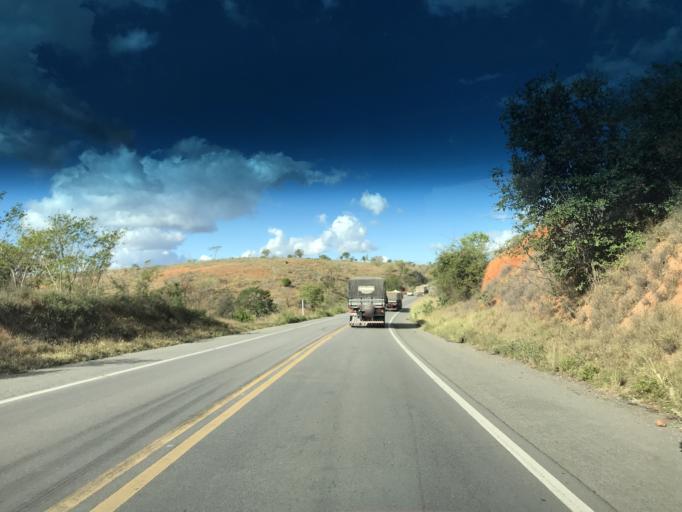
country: BR
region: Bahia
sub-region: Ruy Barbosa
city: Terra Nova
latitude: -12.4424
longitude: -40.8241
